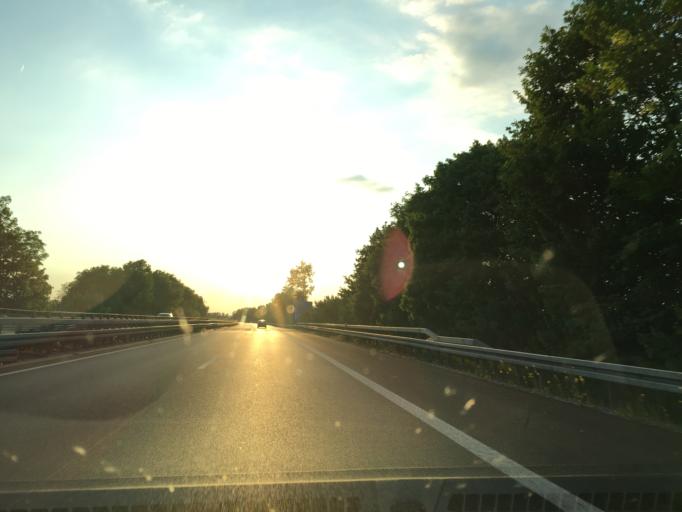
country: DE
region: North Rhine-Westphalia
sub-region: Regierungsbezirk Detmold
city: Rodinghausen
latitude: 52.1962
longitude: 8.4804
